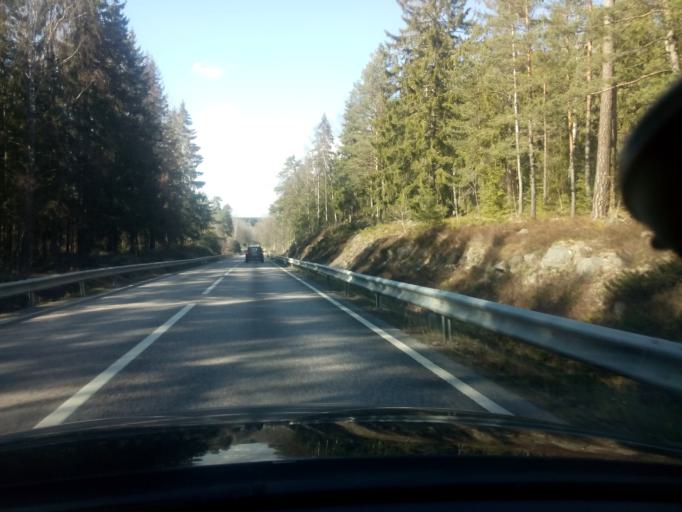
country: SE
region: Soedermanland
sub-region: Strangnas Kommun
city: Akers Styckebruk
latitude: 59.2492
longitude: 16.9413
